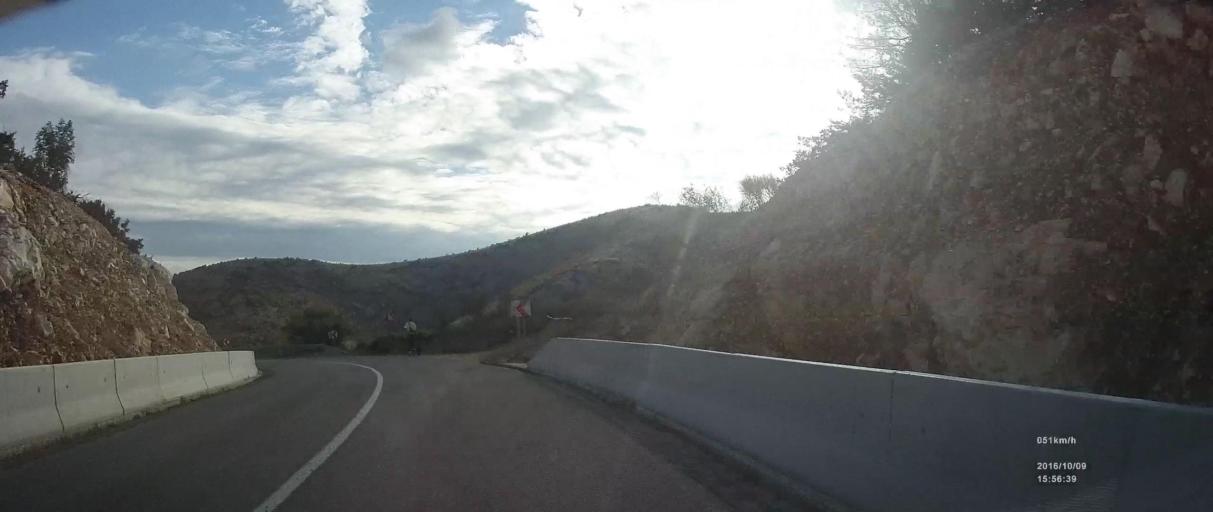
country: HR
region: Splitsko-Dalmatinska
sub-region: Grad Trogir
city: Trogir
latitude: 43.5769
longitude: 16.2326
